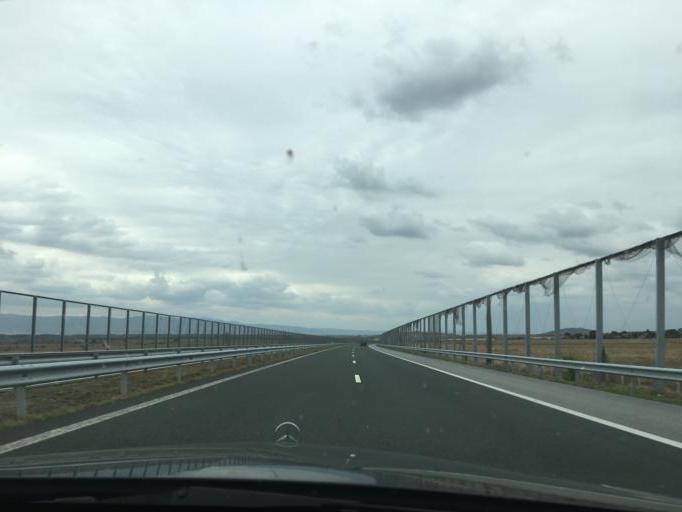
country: BG
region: Yambol
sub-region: Obshtina Yambol
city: Yambol
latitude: 42.5260
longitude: 26.3890
